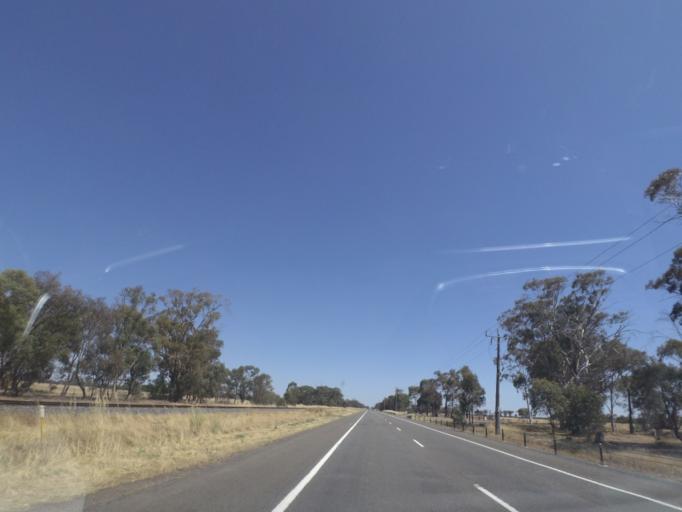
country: AU
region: Victoria
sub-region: Greater Shepparton
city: Shepparton
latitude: -36.2442
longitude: 145.4319
